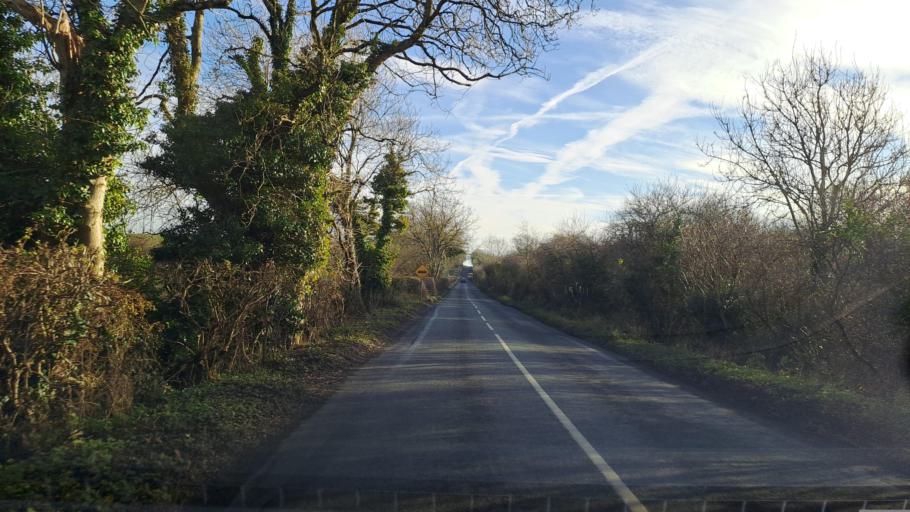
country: IE
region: Ulster
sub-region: An Cabhan
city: Kingscourt
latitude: 53.8802
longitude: -6.7296
